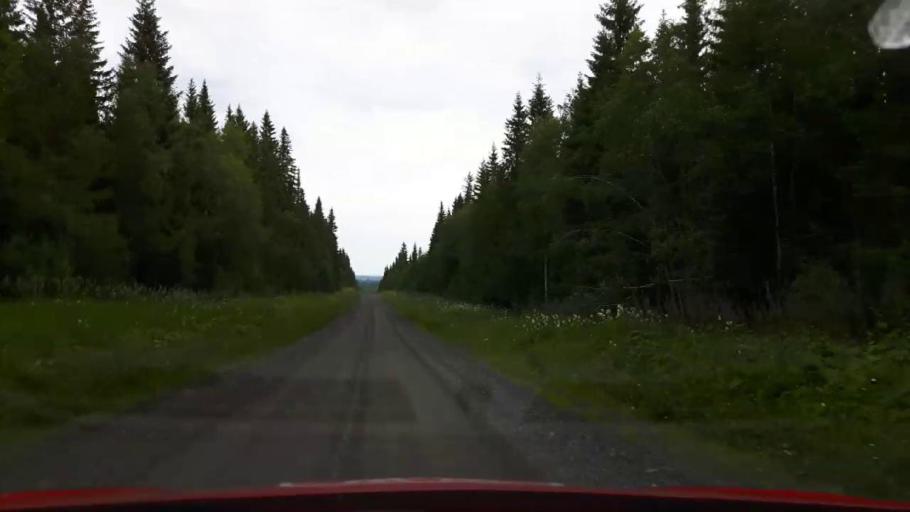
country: SE
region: Jaemtland
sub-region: OEstersunds Kommun
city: Lit
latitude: 63.3873
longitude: 15.2051
